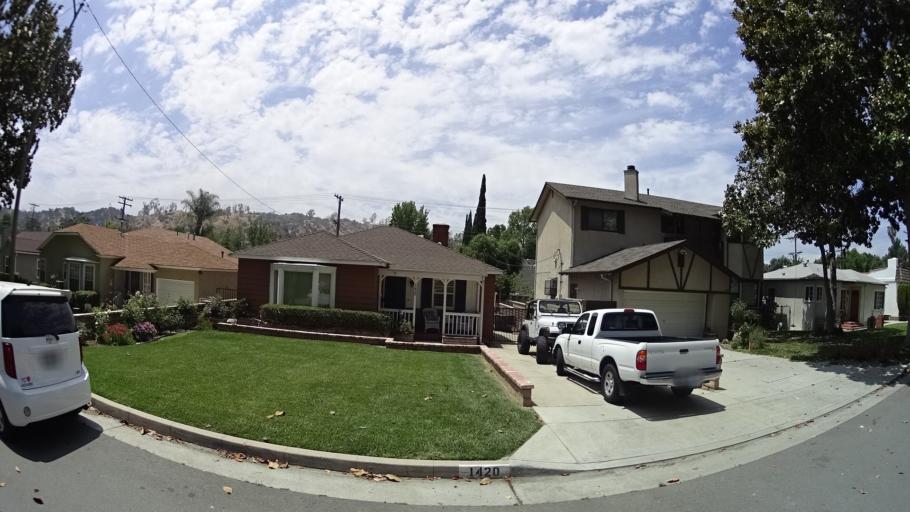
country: US
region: California
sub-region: Los Angeles County
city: Burbank
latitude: 34.1593
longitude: -118.2939
